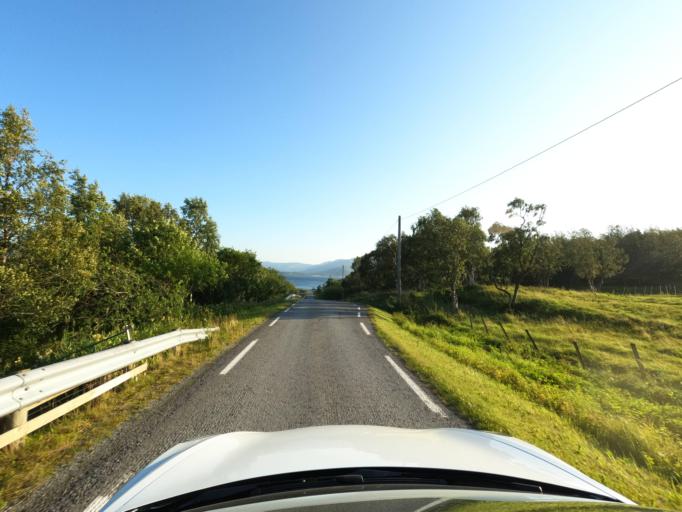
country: NO
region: Troms
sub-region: Skanland
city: Evenskjer
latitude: 68.4583
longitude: 16.6944
